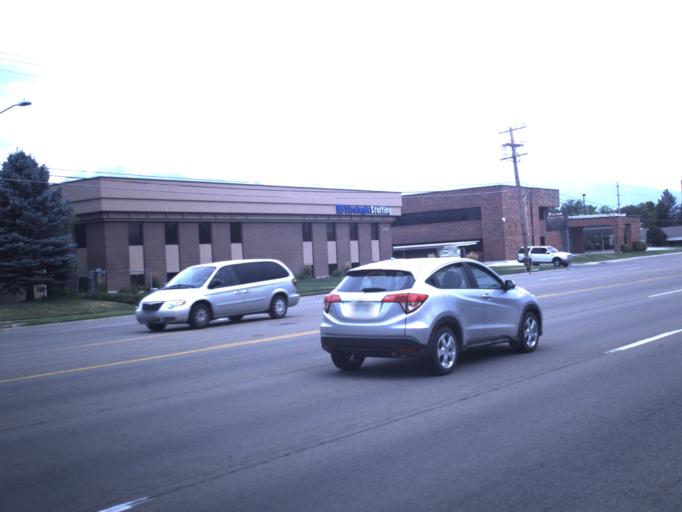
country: US
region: Utah
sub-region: Salt Lake County
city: Millcreek
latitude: 40.6899
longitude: -111.8716
